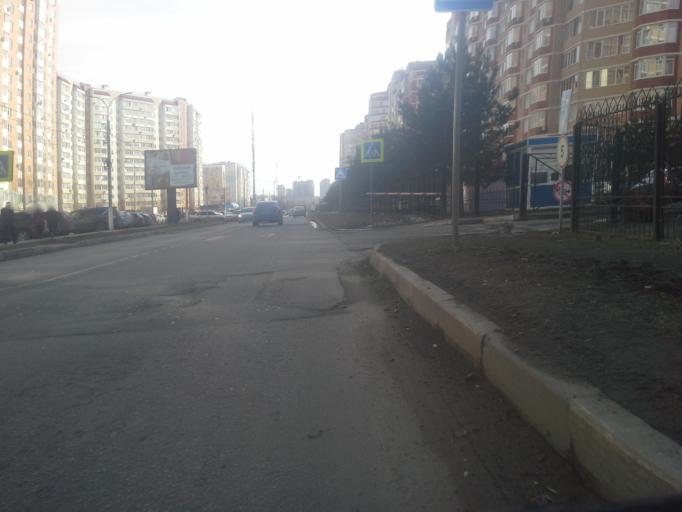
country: RU
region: Moskovskaya
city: Shcherbinka
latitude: 55.4715
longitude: 37.5452
